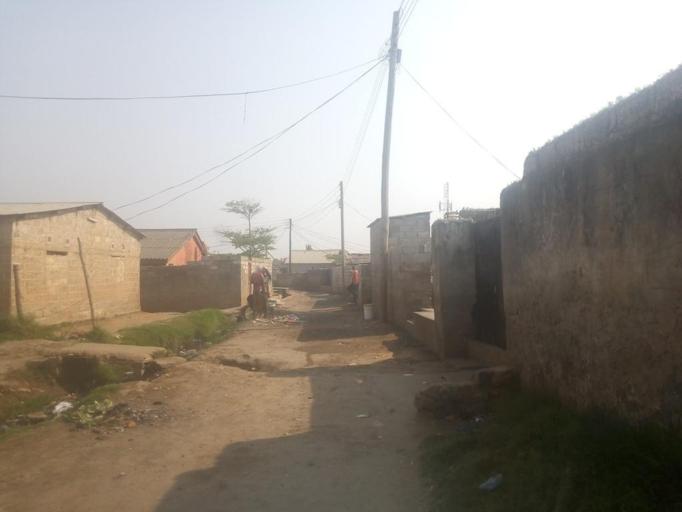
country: ZM
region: Lusaka
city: Lusaka
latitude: -15.4070
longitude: 28.3612
